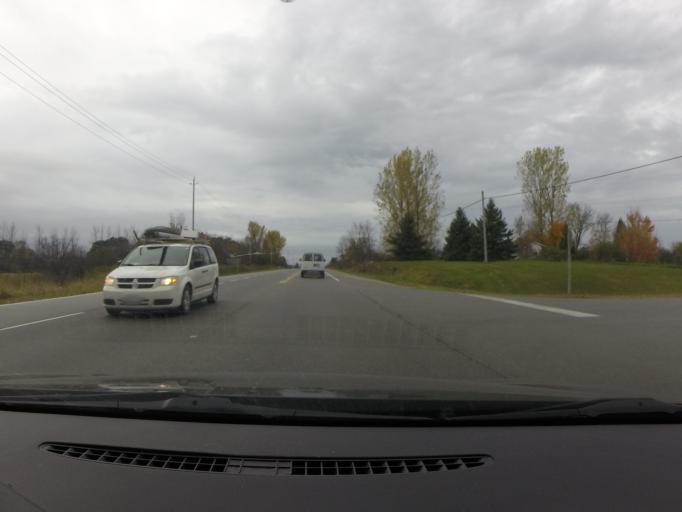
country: CA
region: Ontario
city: Perth
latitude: 44.9416
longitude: -76.2390
